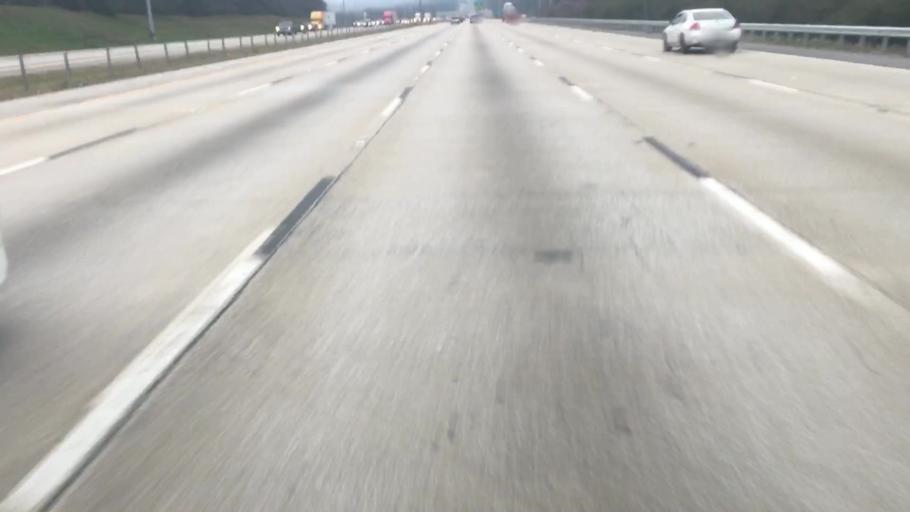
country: US
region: Alabama
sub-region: Jefferson County
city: Hoover
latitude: 33.3882
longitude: -86.7988
